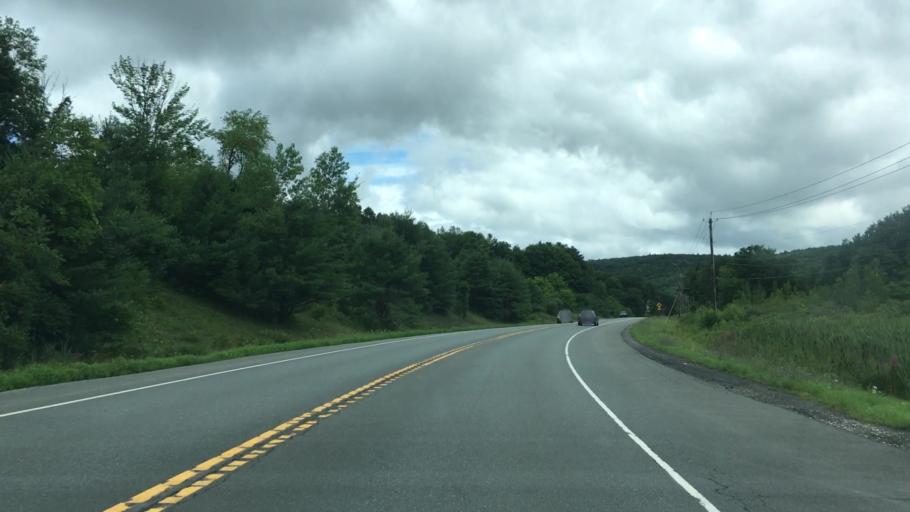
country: US
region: New York
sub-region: Rensselaer County
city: Hoosick Falls
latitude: 42.8454
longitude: -73.3880
